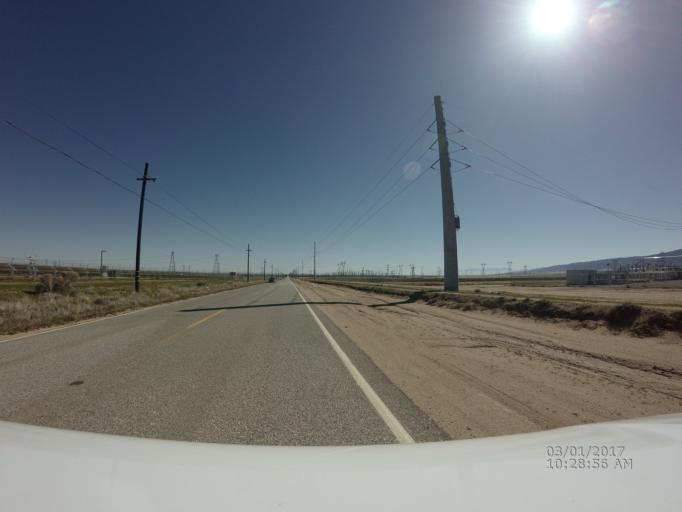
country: US
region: California
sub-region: Los Angeles County
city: Leona Valley
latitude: 34.6892
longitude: -118.3148
